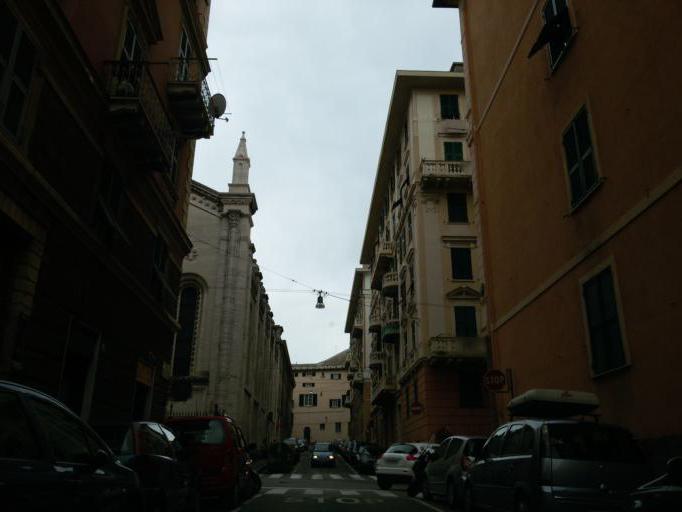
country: IT
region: Liguria
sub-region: Provincia di Genova
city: San Teodoro
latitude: 44.4143
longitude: 8.8906
